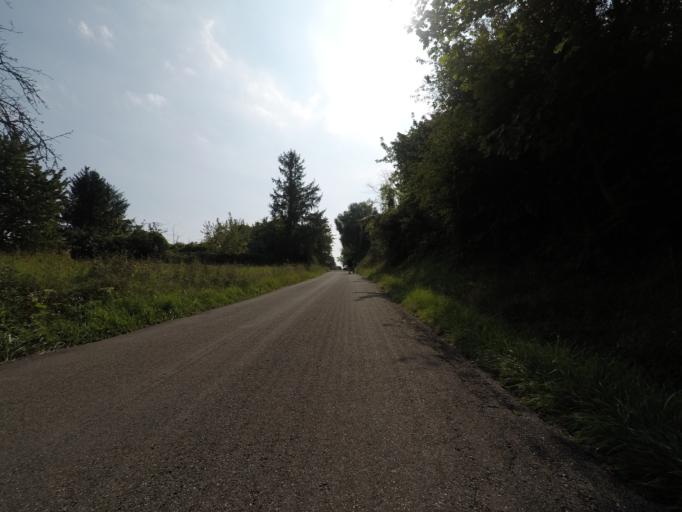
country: DE
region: Baden-Wuerttemberg
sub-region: Regierungsbezirk Stuttgart
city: Weinstadt-Endersbach
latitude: 48.8053
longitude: 9.4018
